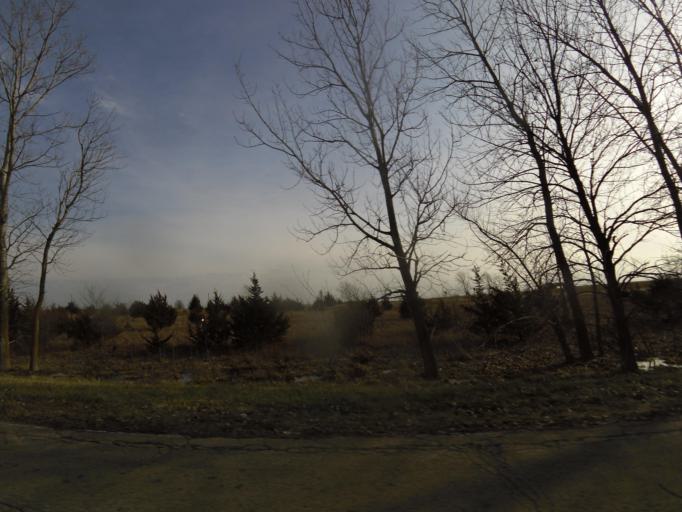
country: US
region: Illinois
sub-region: Macon County
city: Macon
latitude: 39.7685
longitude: -88.9827
